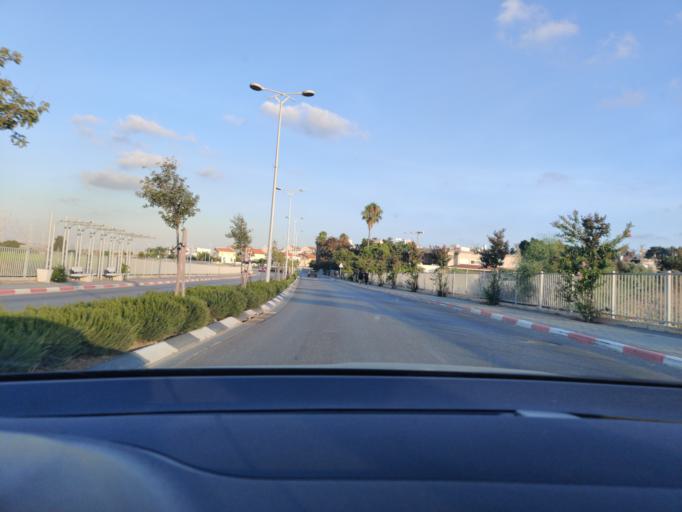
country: IL
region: Central District
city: Elyakhin
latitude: 32.4386
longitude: 34.9390
